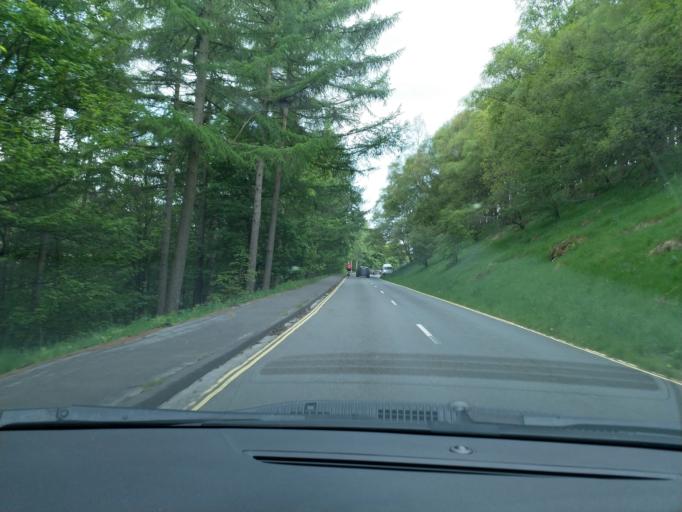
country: GB
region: England
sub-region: Derbyshire
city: Hope Valley
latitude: 53.3826
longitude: -1.7184
